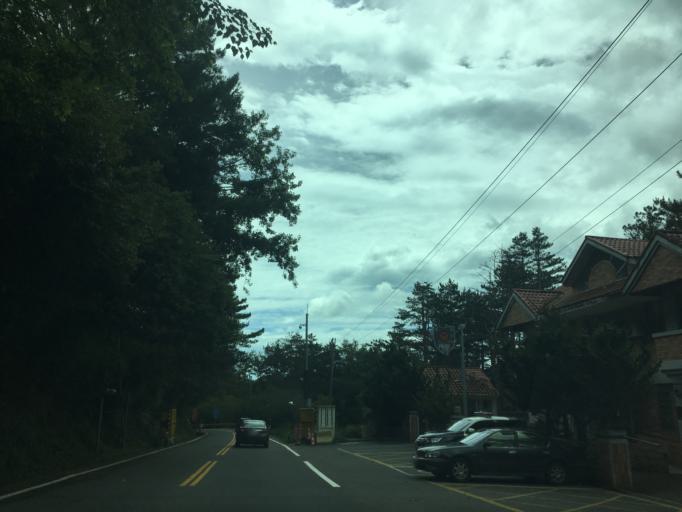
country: TW
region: Taiwan
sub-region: Hualien
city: Hualian
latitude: 24.1866
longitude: 121.3387
